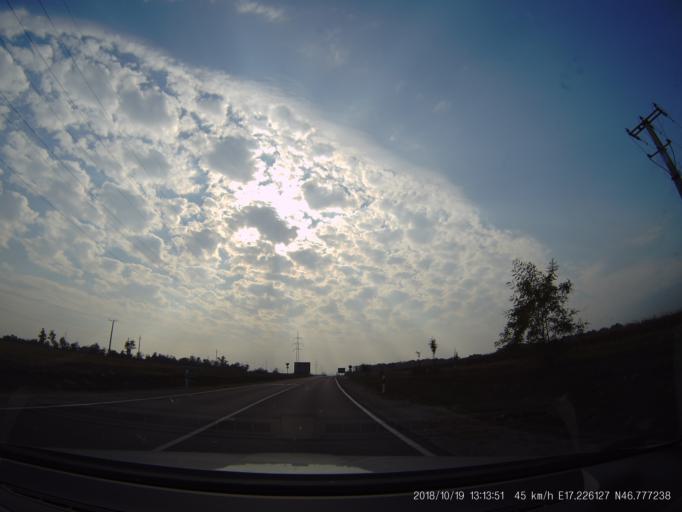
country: HU
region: Zala
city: Keszthely
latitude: 46.7773
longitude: 17.2262
